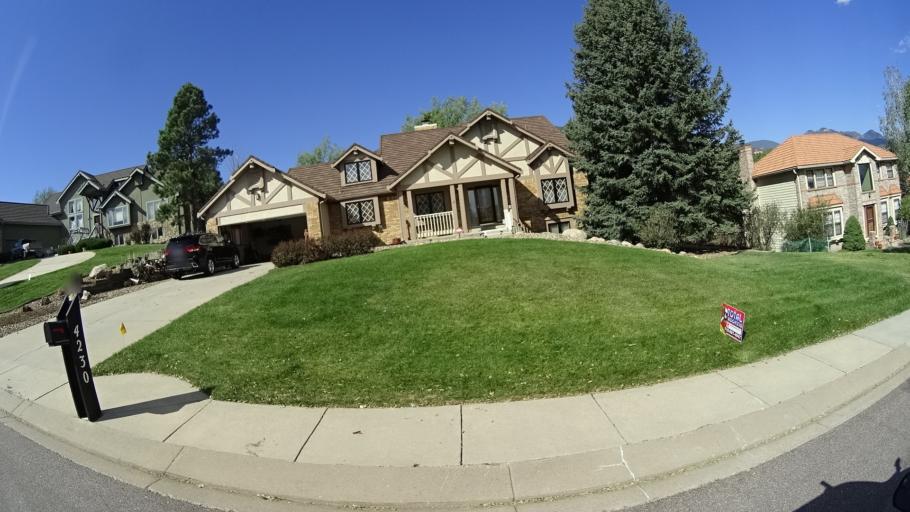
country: US
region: Colorado
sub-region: El Paso County
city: Stratmoor
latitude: 38.7682
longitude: -104.8194
